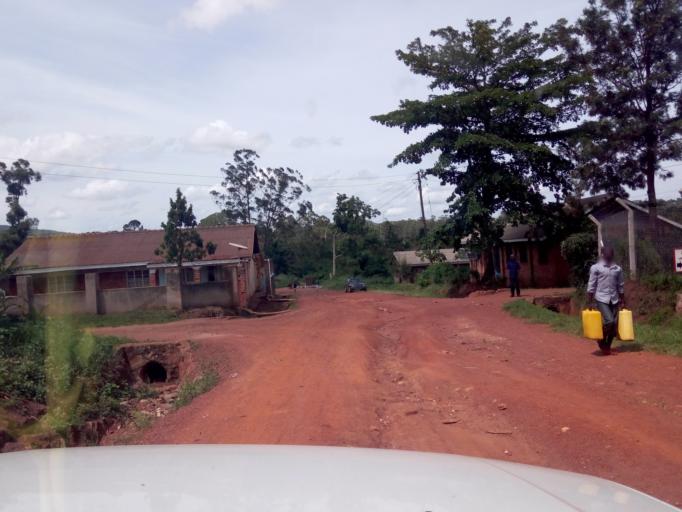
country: UG
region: Western Region
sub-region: Masindi District
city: Masindi
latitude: 1.6807
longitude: 31.7152
